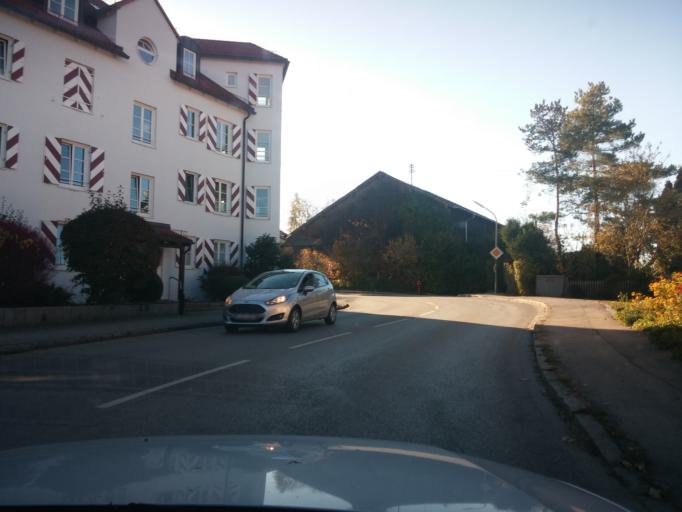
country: DE
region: Bavaria
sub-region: Upper Bavaria
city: Egmating
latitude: 48.0029
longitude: 11.7958
